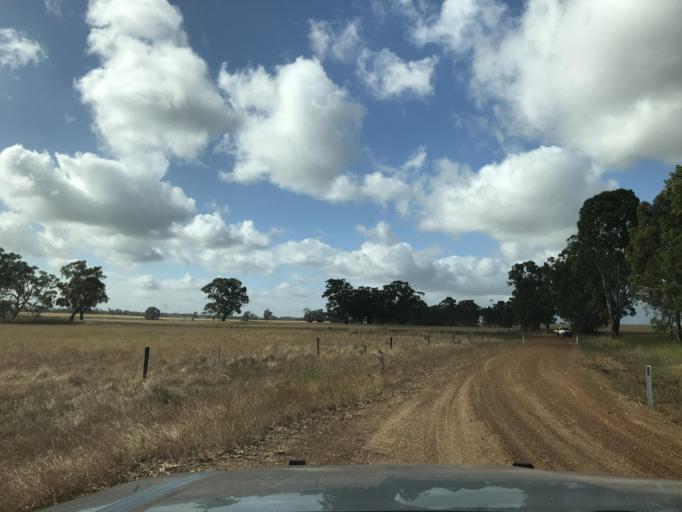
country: AU
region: South Australia
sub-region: Naracoorte and Lucindale
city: Naracoorte
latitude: -36.9285
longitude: 141.3972
